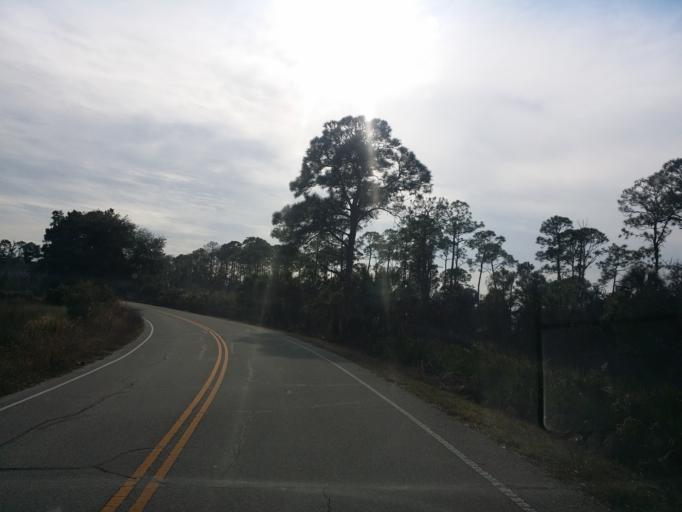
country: US
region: Florida
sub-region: Wakulla County
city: Crawfordville
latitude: 30.0943
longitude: -84.1654
